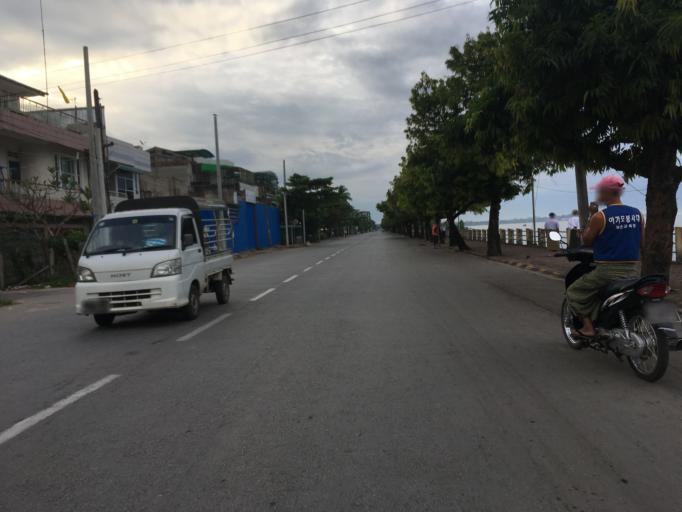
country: MM
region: Mon
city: Mawlamyine
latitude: 16.4769
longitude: 97.6197
